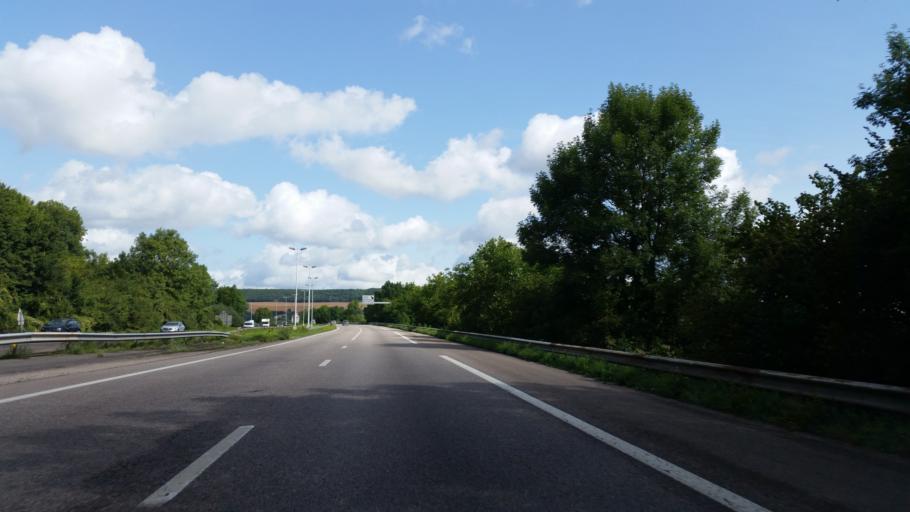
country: FR
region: Lorraine
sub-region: Departement de Meurthe-et-Moselle
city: Belleville
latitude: 48.8079
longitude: 6.1138
